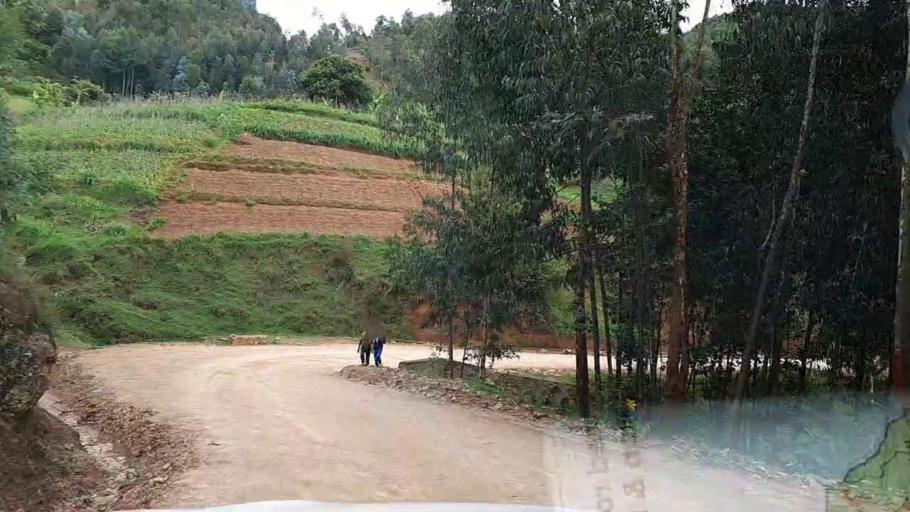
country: RW
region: Southern Province
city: Nzega
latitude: -2.4039
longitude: 29.4546
